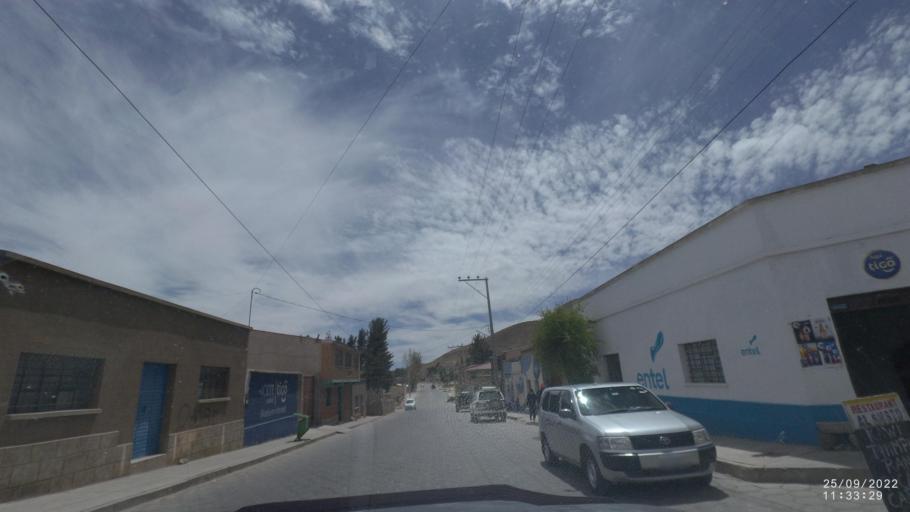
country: BO
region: Oruro
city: Challapata
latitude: -19.0104
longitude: -66.7763
